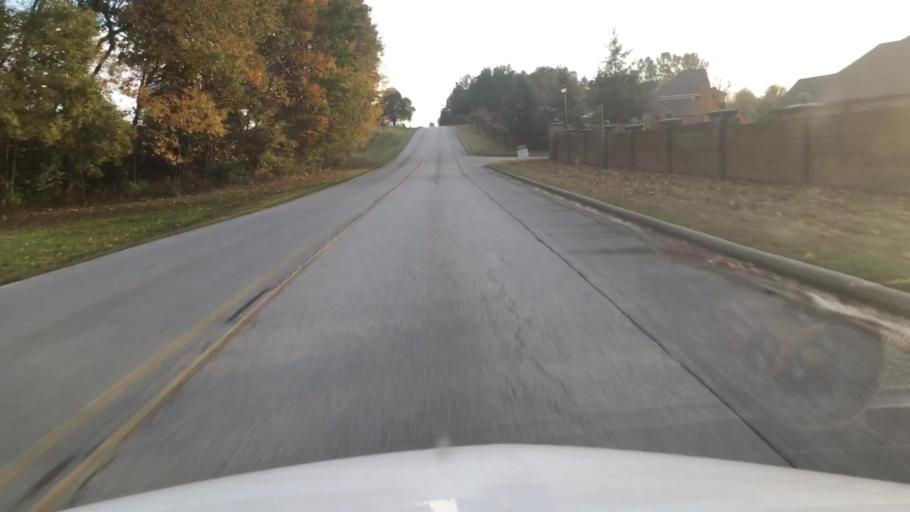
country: US
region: Arkansas
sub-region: Washington County
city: Tontitown
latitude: 36.1873
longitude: -94.2320
